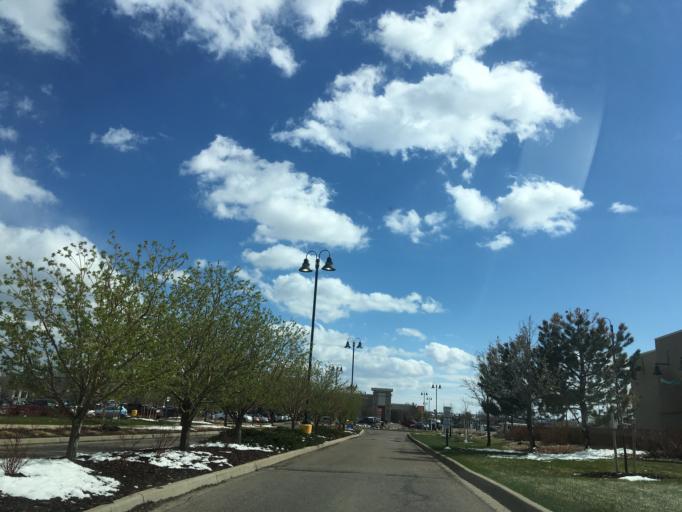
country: US
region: Colorado
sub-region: Adams County
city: Northglenn
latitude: 39.9428
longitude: -104.9916
